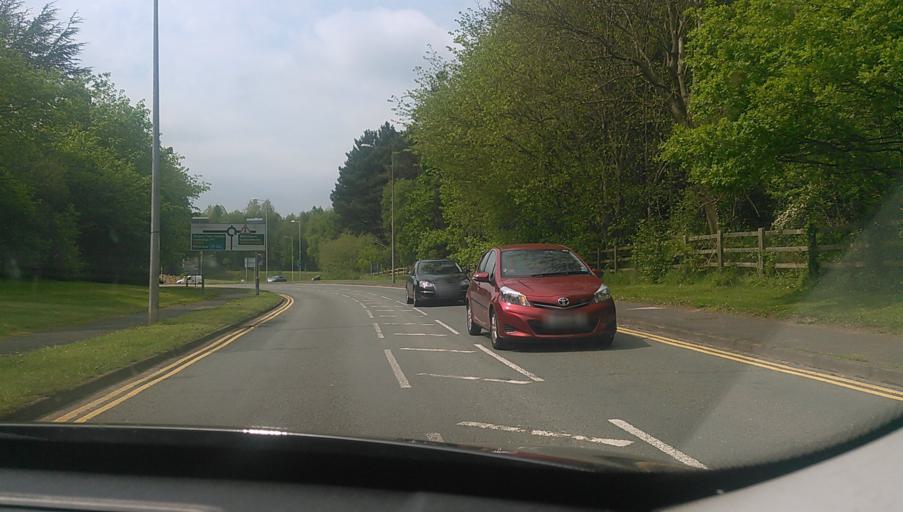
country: GB
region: England
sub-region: Telford and Wrekin
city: Wellington
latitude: 52.7103
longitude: -2.5103
